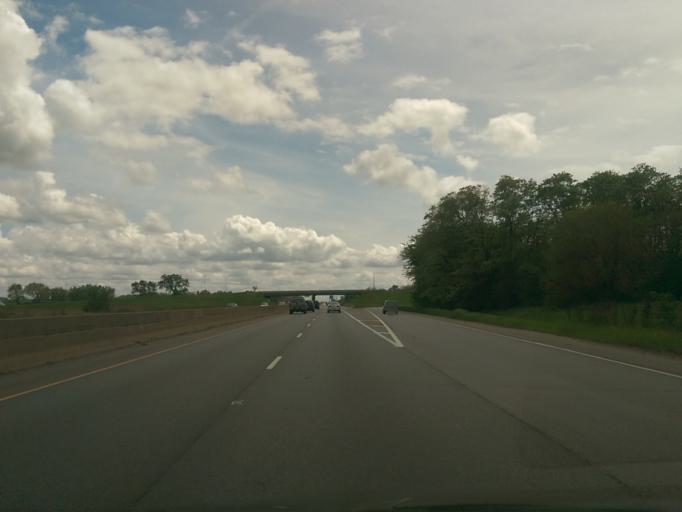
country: US
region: Indiana
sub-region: Lake County
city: Highland
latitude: 41.5908
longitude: -87.4330
